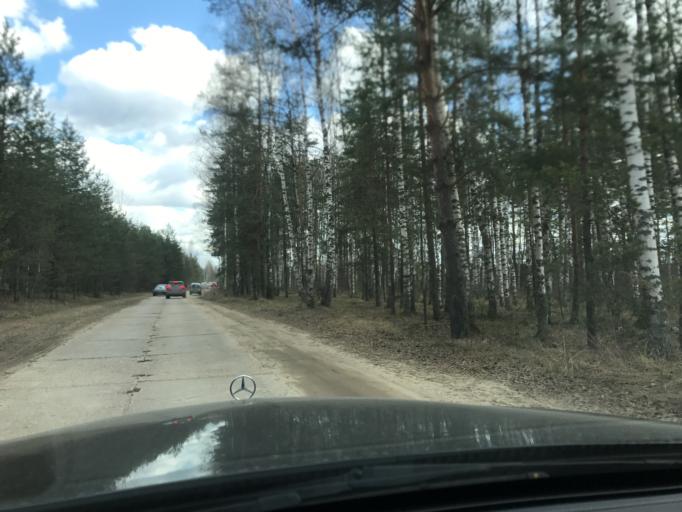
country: RU
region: Vladimir
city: Pokrov
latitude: 55.8506
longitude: 39.1770
